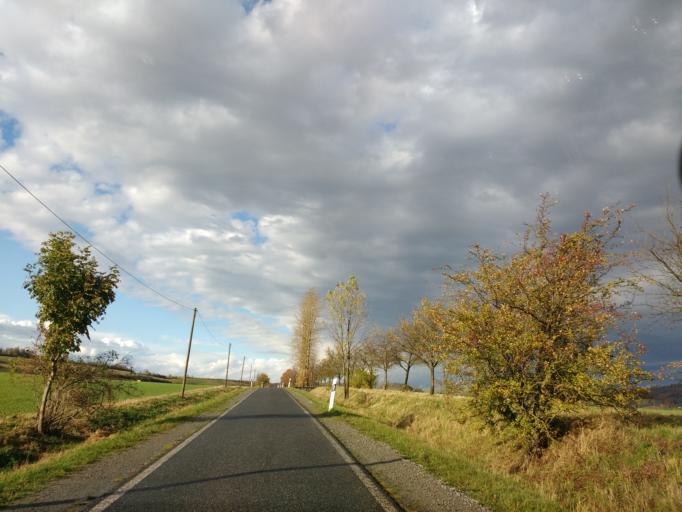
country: DE
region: Thuringia
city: Worbis
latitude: 51.4052
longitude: 10.3590
